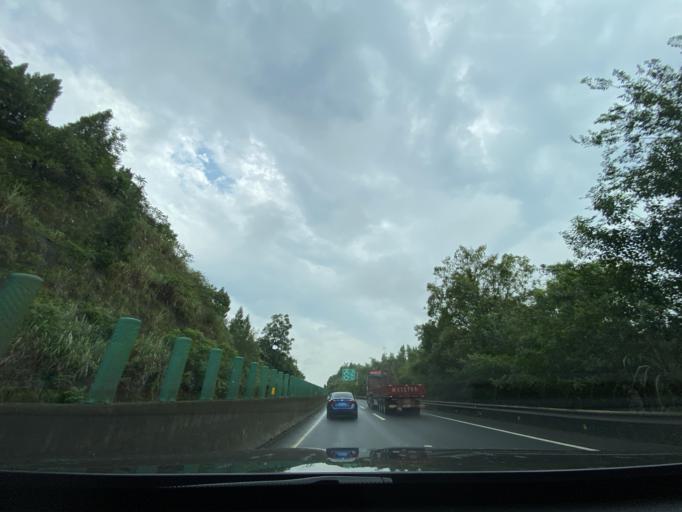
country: CN
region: Sichuan
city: Yanjiang
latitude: 30.1170
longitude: 104.5987
